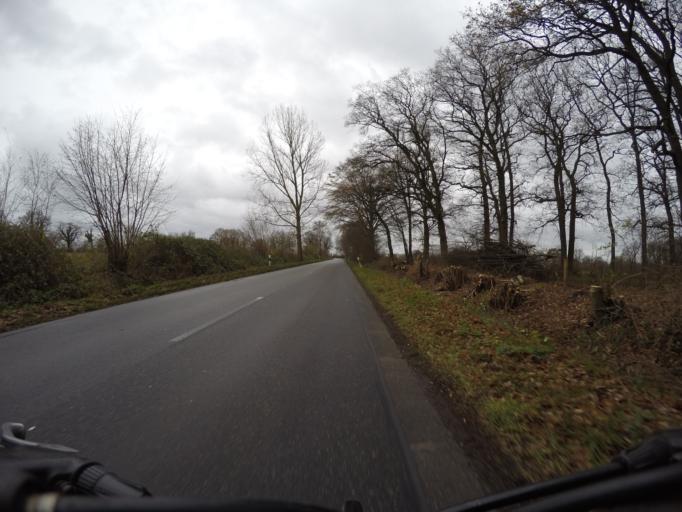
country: DE
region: Schleswig-Holstein
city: Hasloh
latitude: 53.6957
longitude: 9.8696
